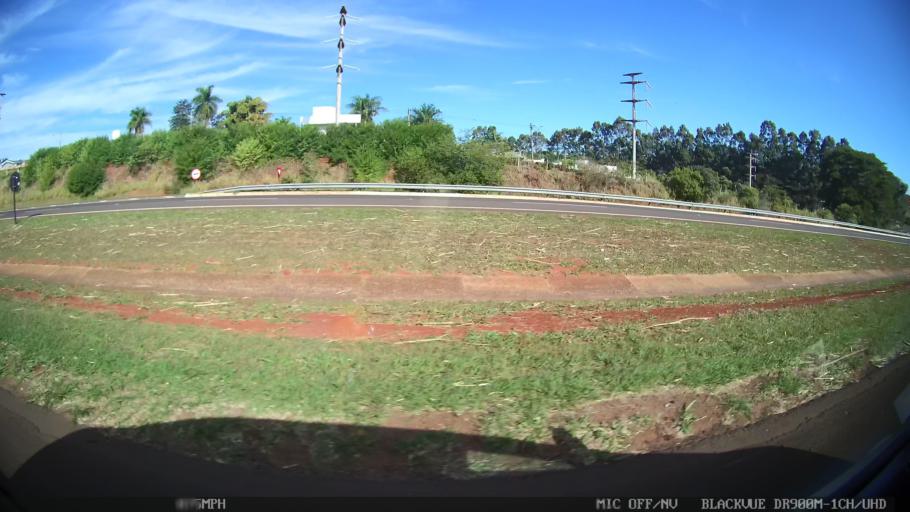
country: BR
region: Sao Paulo
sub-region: Araraquara
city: Araraquara
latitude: -21.8149
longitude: -48.1691
